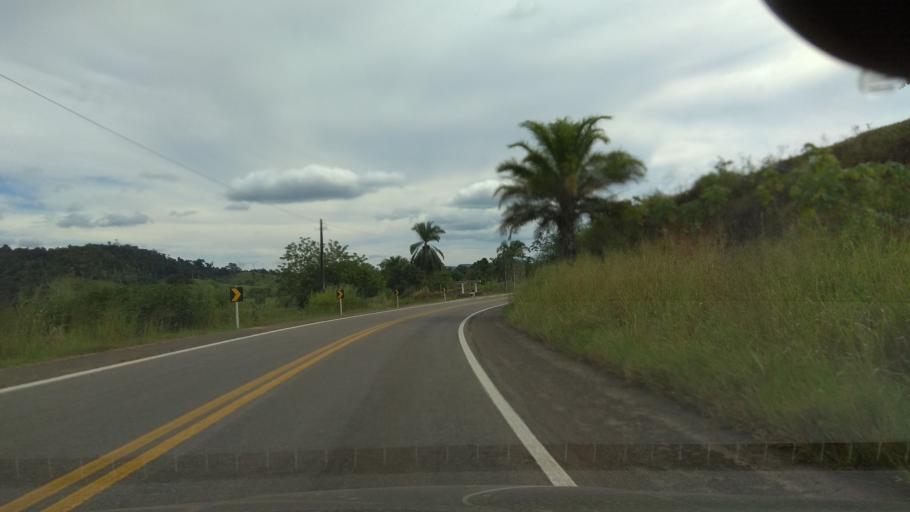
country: BR
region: Bahia
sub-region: Ubata
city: Ubata
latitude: -14.2105
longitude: -39.5789
